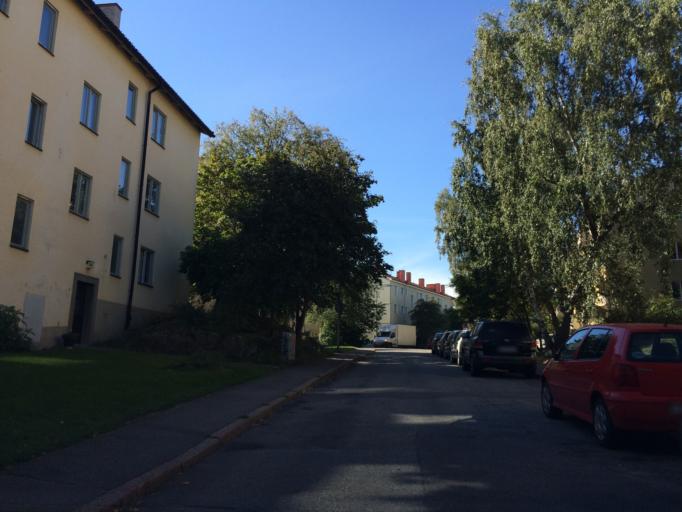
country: SE
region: Stockholm
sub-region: Stockholms Kommun
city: Arsta
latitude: 59.3039
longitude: 17.9987
